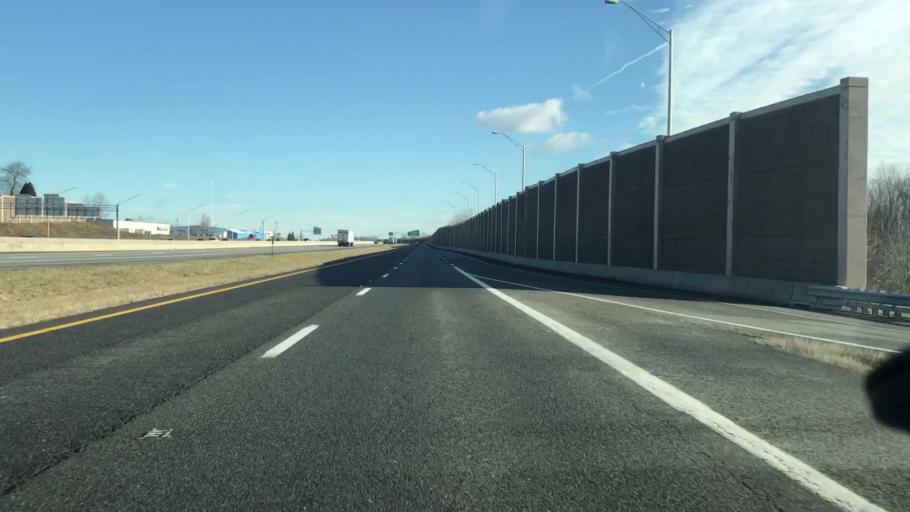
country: US
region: Virginia
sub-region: Montgomery County
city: Christiansburg
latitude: 37.1304
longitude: -80.3663
